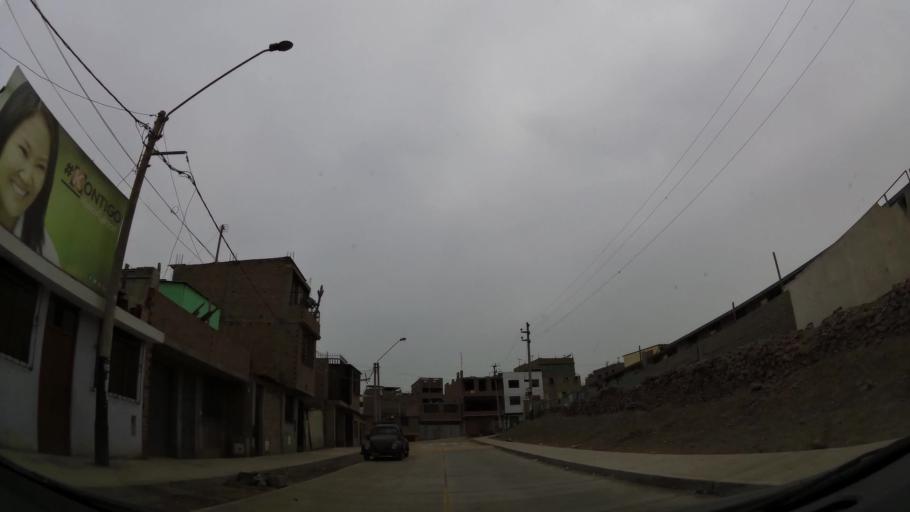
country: PE
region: Lima
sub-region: Lima
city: Surco
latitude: -12.1913
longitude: -76.9762
